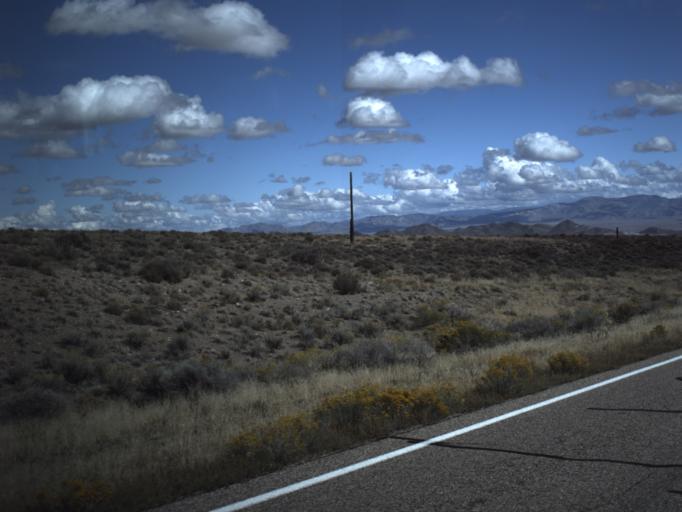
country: US
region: Utah
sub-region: Beaver County
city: Milford
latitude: 38.4500
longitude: -113.1968
